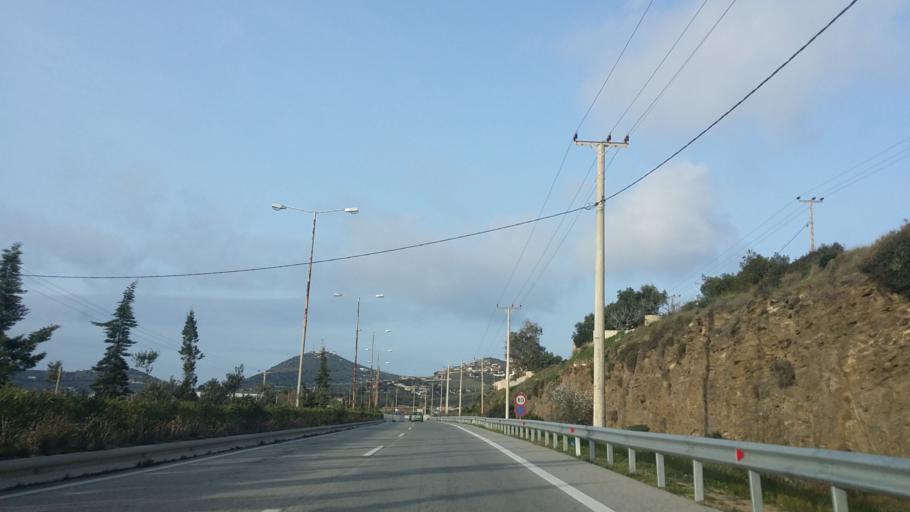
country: GR
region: Attica
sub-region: Nomarchia Anatolikis Attikis
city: Lavrio
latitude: 37.7756
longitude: 24.0551
